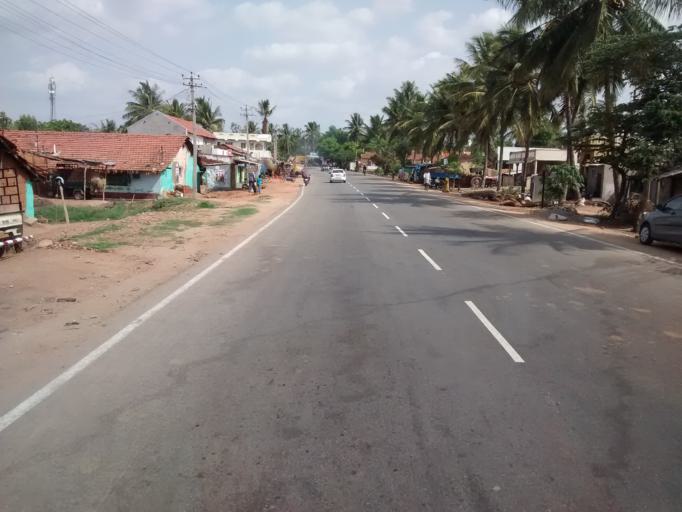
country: IN
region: Karnataka
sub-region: Mysore
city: Hunsur
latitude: 12.3675
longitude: 76.4177
